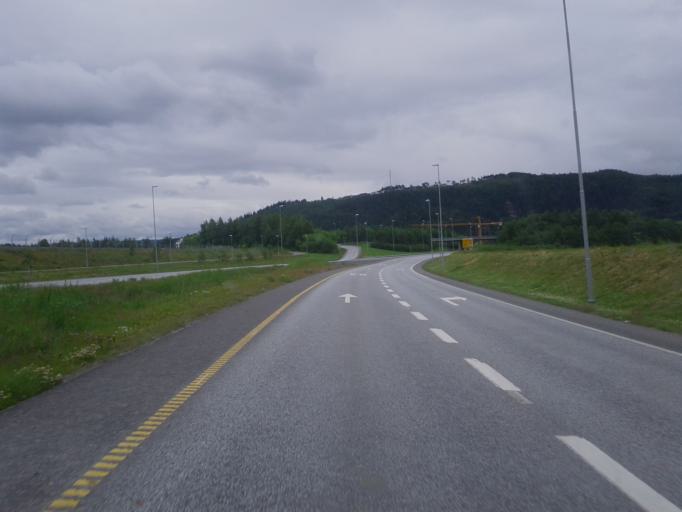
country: NO
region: Nord-Trondelag
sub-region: Stjordal
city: Stjordal
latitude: 63.4544
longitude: 10.9096
